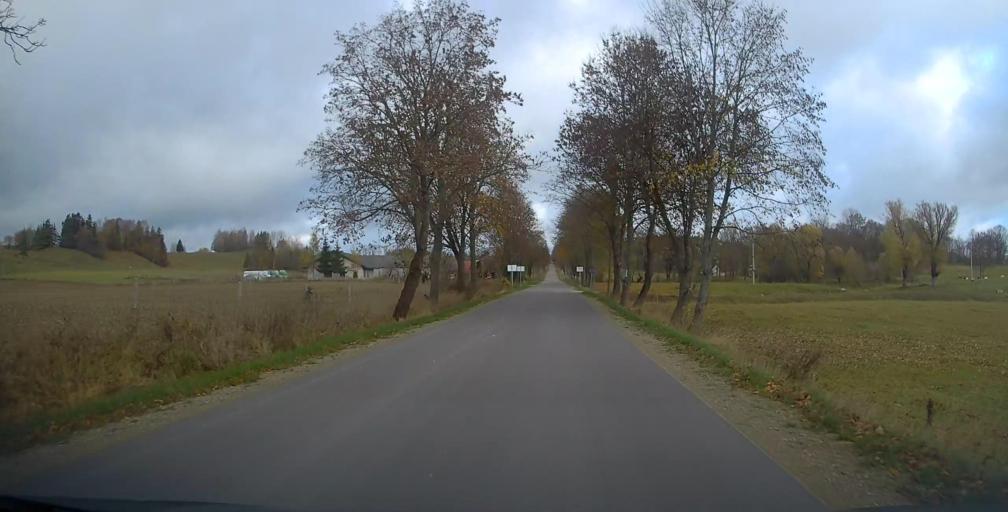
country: PL
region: Podlasie
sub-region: Suwalki
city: Suwalki
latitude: 54.3027
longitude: 22.8793
